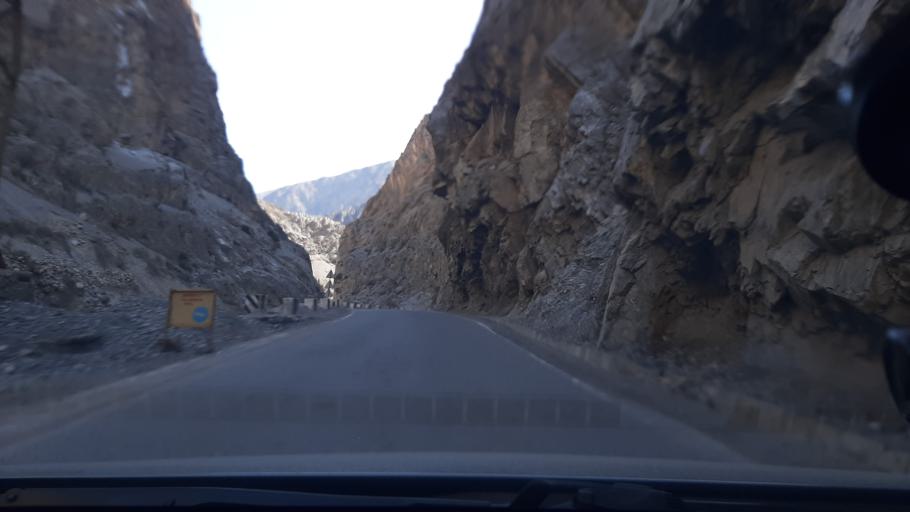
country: TJ
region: Viloyati Sughd
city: Ayni
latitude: 39.3129
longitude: 68.5350
